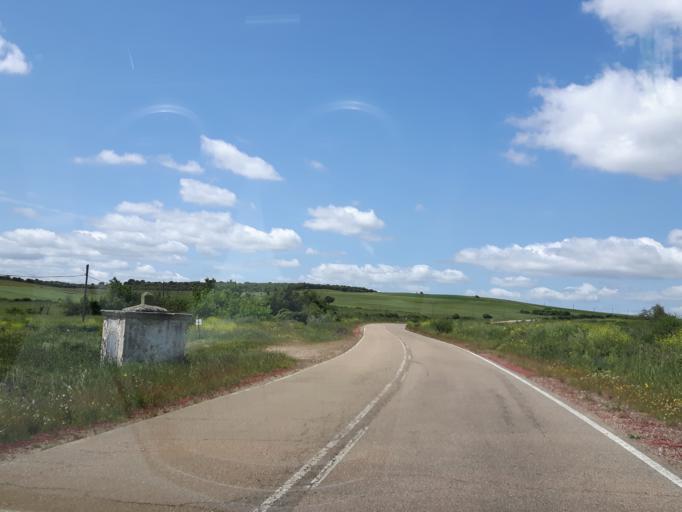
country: ES
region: Castille and Leon
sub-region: Provincia de Salamanca
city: Villar de Ciervo
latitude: 40.7286
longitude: -6.7510
